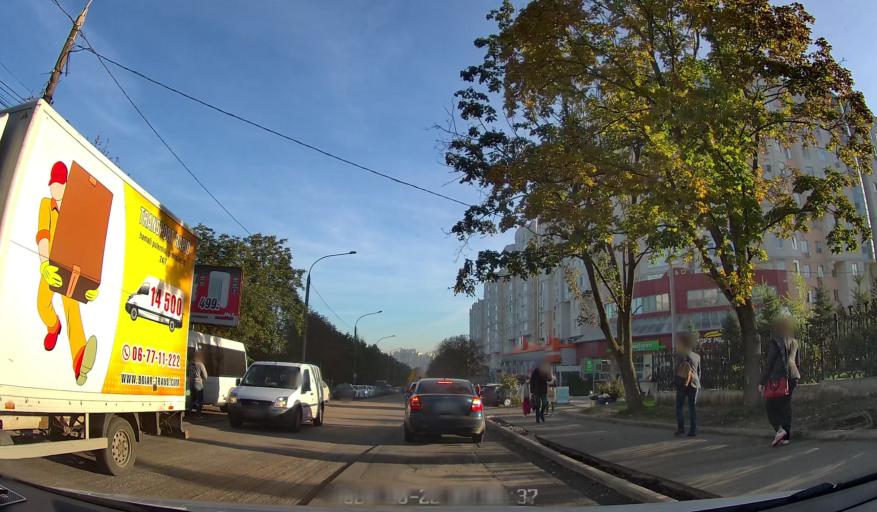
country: MD
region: Chisinau
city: Chisinau
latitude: 46.9959
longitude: 28.8331
